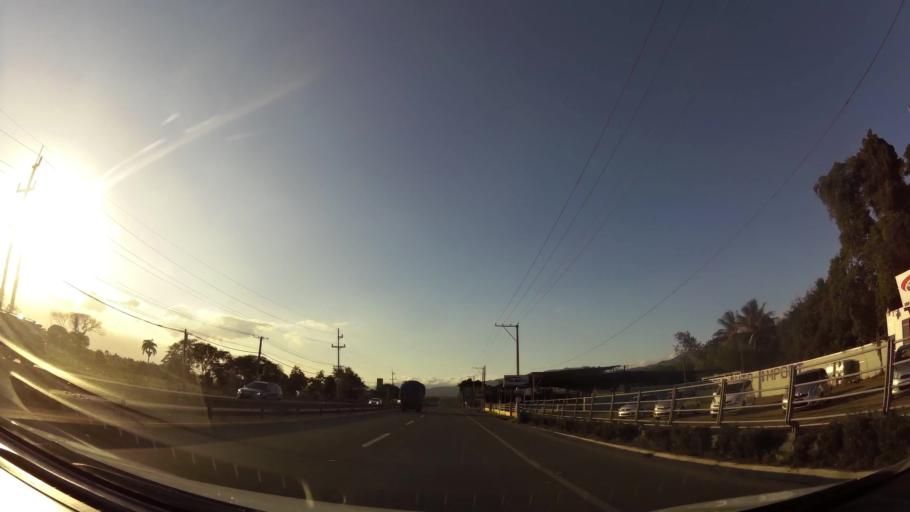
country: DO
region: Santiago
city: Palmar Arriba
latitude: 19.5123
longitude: -70.7590
